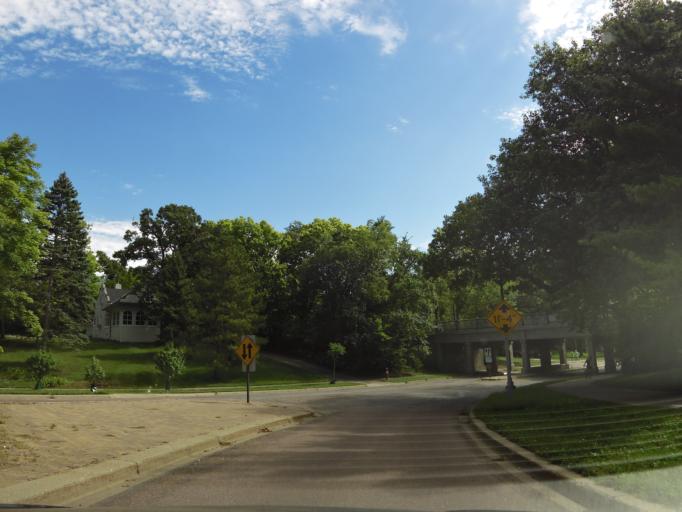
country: US
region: Minnesota
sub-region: Hennepin County
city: Saint Louis Park
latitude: 44.9509
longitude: -93.3053
